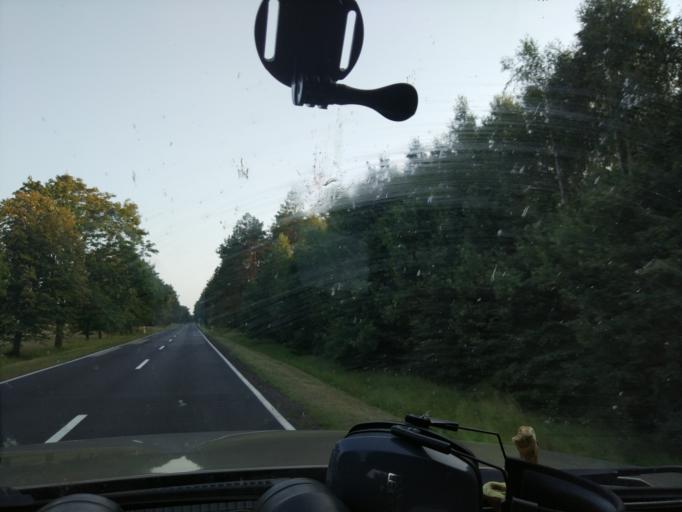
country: PL
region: Warmian-Masurian Voivodeship
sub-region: Powiat szczycienski
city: Wielbark
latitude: 53.3396
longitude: 20.9015
